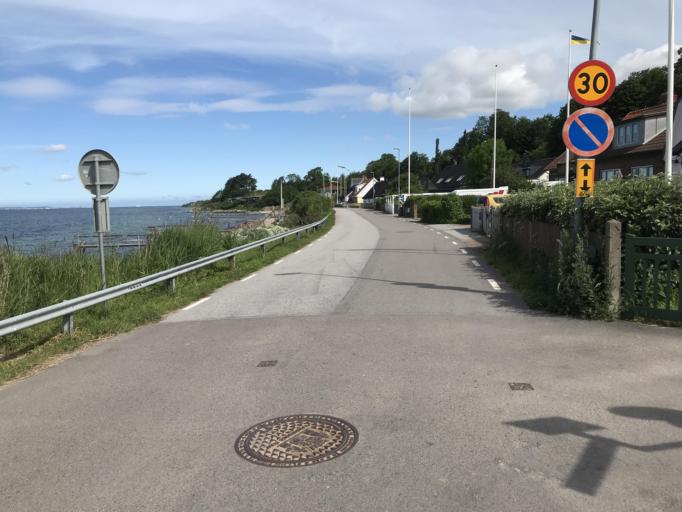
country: SE
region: Skane
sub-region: Helsingborg
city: Rydeback
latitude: 55.9409
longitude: 12.7723
